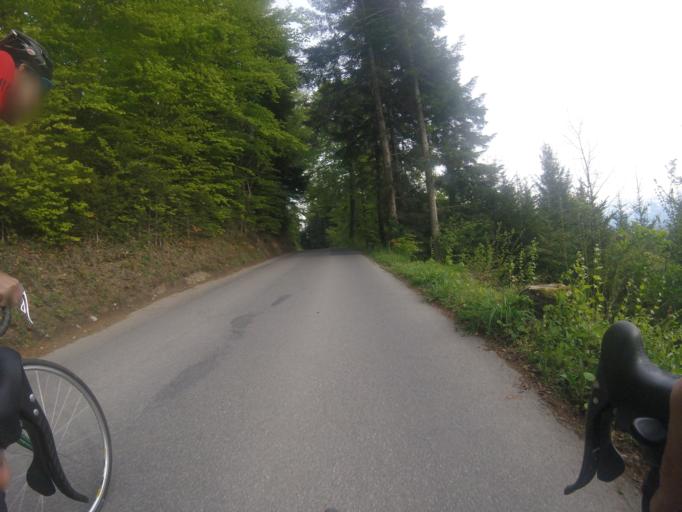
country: CH
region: Lucerne
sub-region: Entlebuch District
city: Oberdiessbach
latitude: 46.8366
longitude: 7.6011
